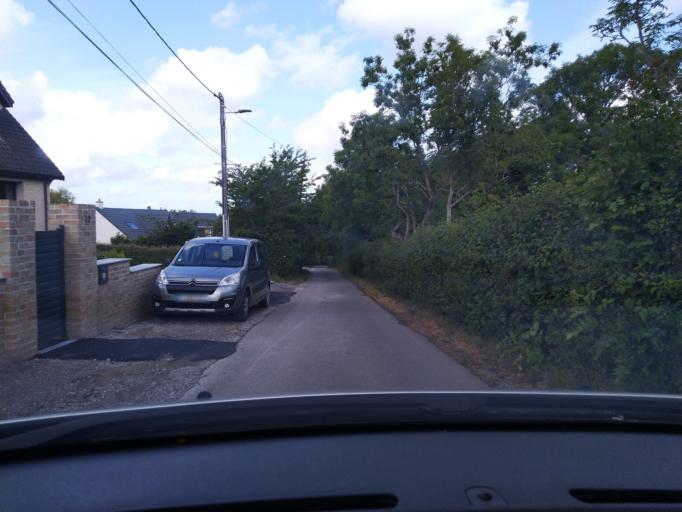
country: FR
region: Nord-Pas-de-Calais
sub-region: Departement du Pas-de-Calais
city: Ferques
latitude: 50.8354
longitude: 1.7591
